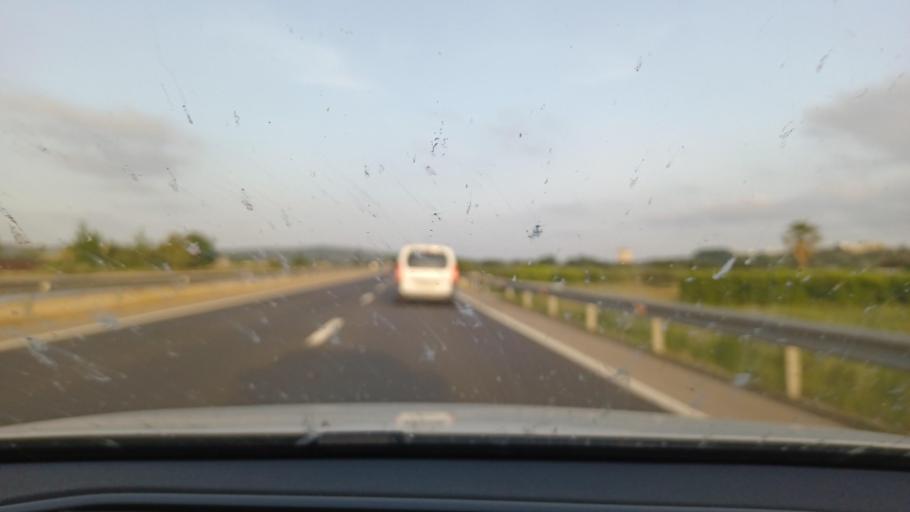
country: ES
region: Catalonia
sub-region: Provincia de Tarragona
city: Masdenverge
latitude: 40.7492
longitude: 0.5522
